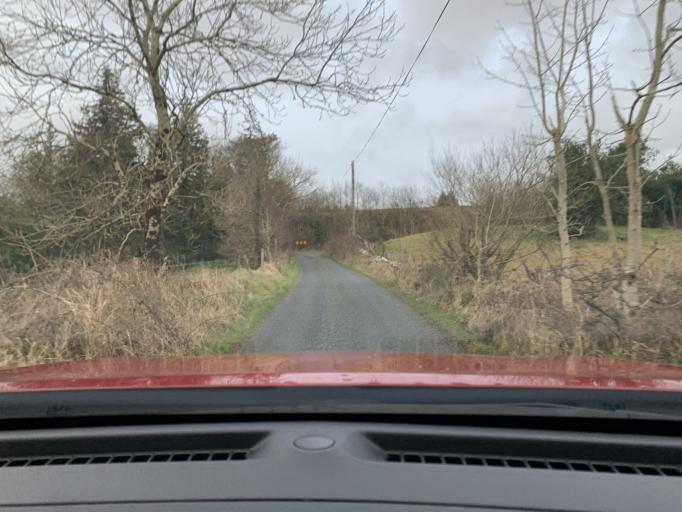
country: IE
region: Connaught
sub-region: Roscommon
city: Boyle
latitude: 53.9783
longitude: -8.4170
